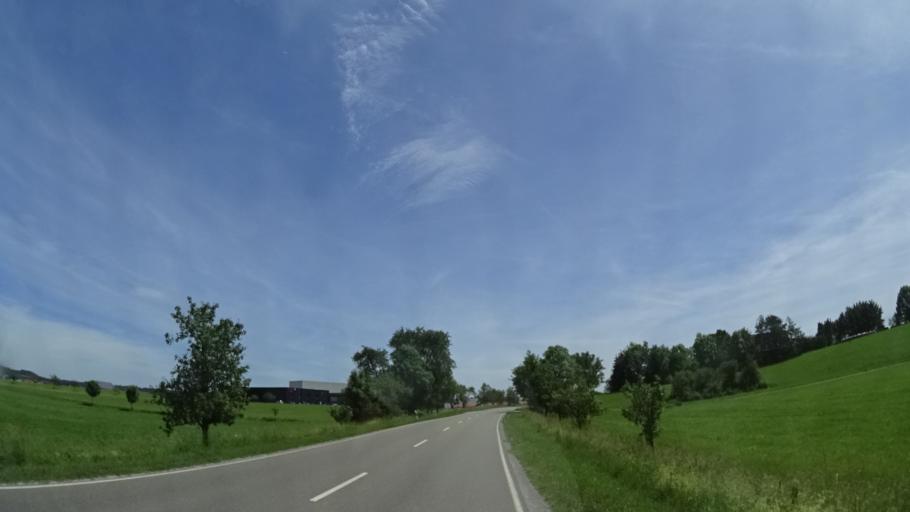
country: DE
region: Baden-Wuerttemberg
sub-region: Regierungsbezirk Stuttgart
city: Obersontheim
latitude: 49.0577
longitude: 9.8786
